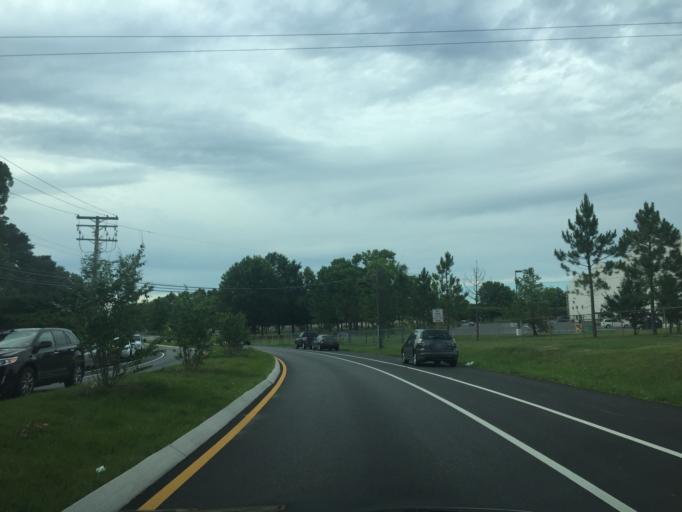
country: US
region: Maryland
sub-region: Baltimore County
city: Middle River
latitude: 39.3265
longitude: -76.4229
